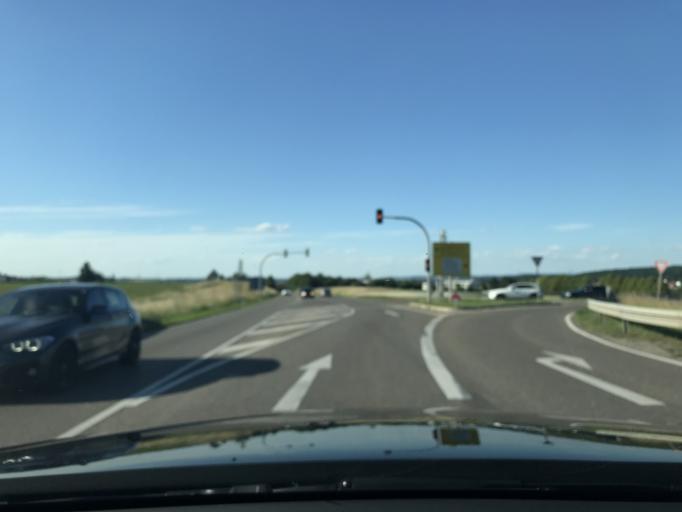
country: DE
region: Baden-Wuerttemberg
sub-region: Regierungsbezirk Stuttgart
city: Stuttgart Muehlhausen
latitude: 48.8379
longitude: 9.2512
